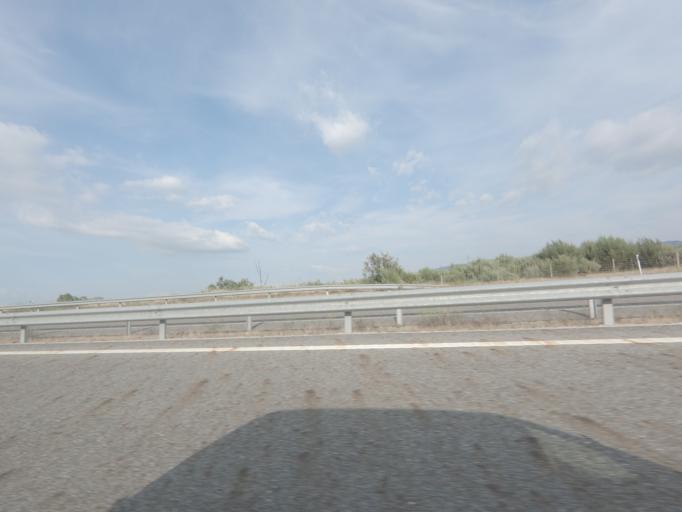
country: PT
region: Vila Real
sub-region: Chaves
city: Chaves
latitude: 41.7382
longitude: -7.5263
